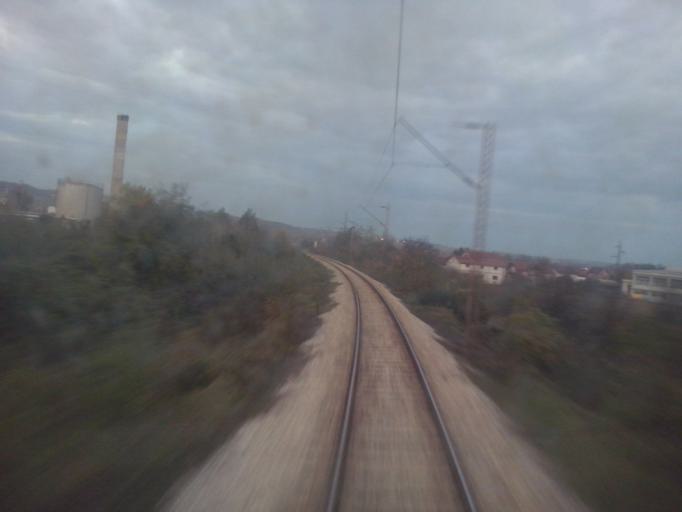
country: RS
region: Central Serbia
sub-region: Kolubarski Okrug
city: Valjevo
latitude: 44.2752
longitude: 19.9236
